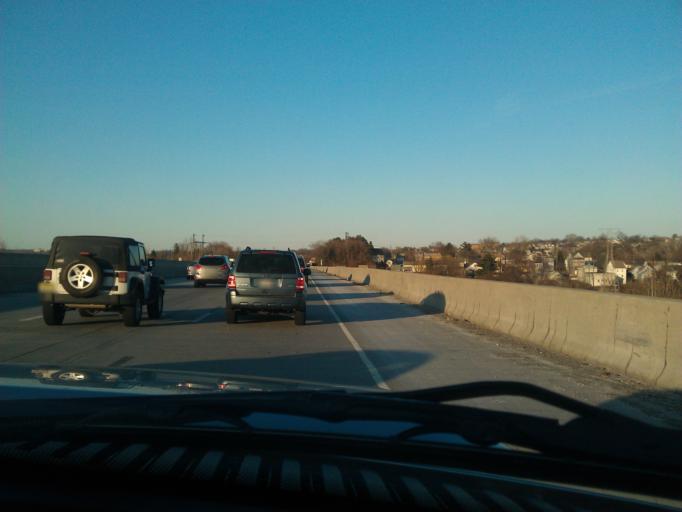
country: US
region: Pennsylvania
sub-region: Montgomery County
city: West Conshohocken
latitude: 40.0768
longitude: -75.3198
